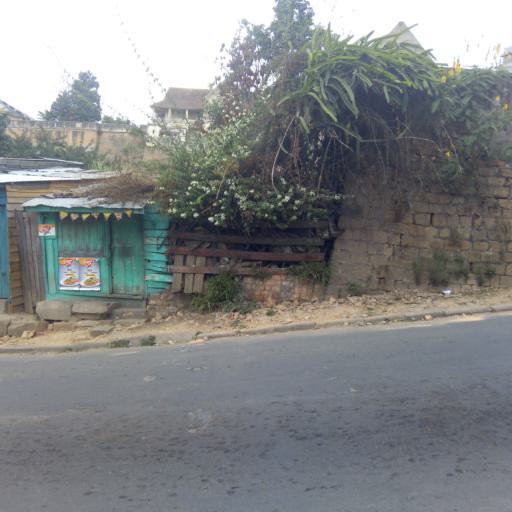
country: MG
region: Analamanga
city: Antananarivo
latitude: -18.9196
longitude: 47.5320
